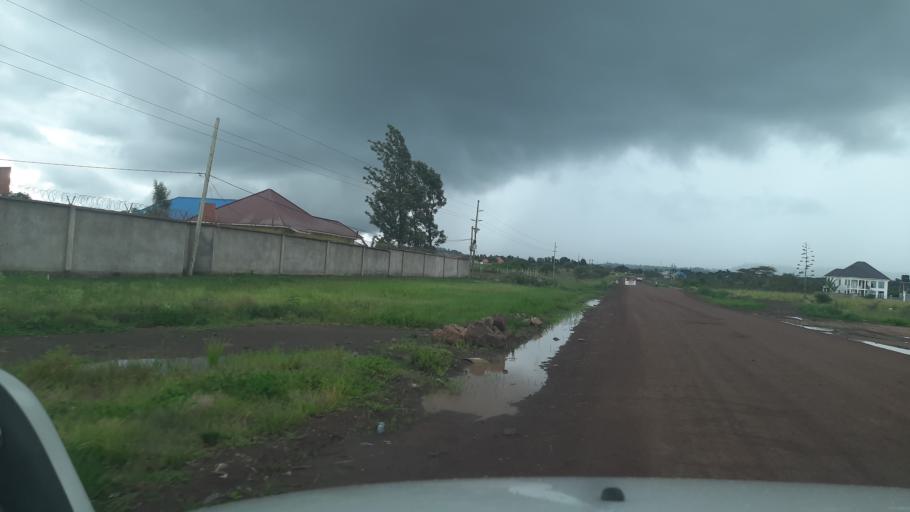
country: TZ
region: Arusha
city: Arusha
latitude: -3.4371
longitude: 36.7394
